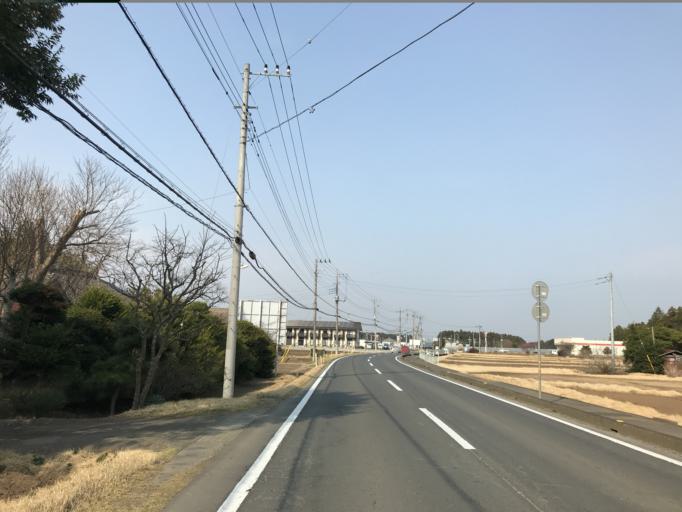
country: JP
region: Ibaraki
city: Okunoya
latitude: 36.2024
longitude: 140.3943
